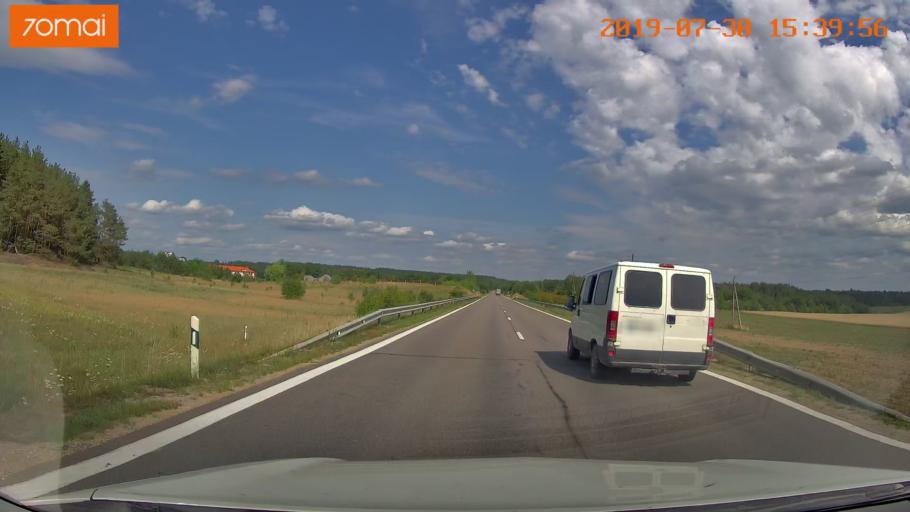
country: LT
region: Vilnius County
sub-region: Trakai
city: Rudiskes
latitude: 54.6032
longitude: 24.8243
